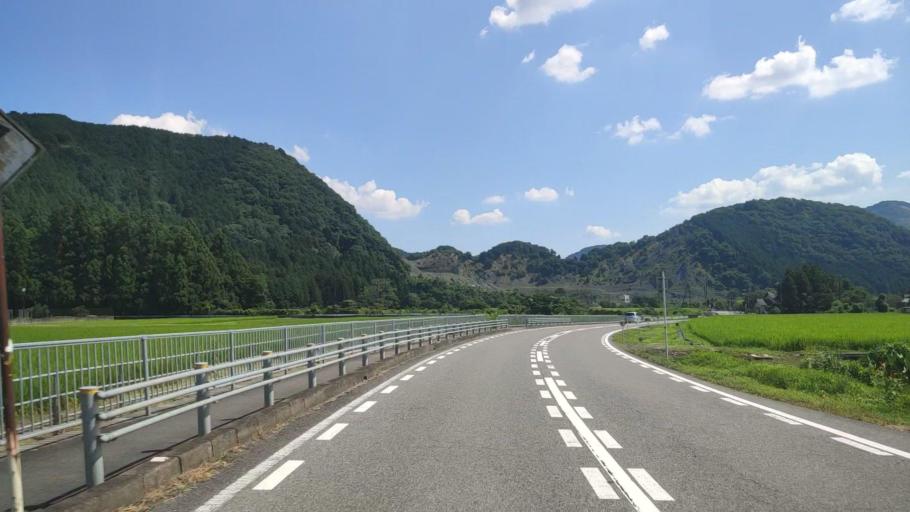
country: JP
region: Gifu
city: Godo
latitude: 35.5337
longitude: 136.6513
